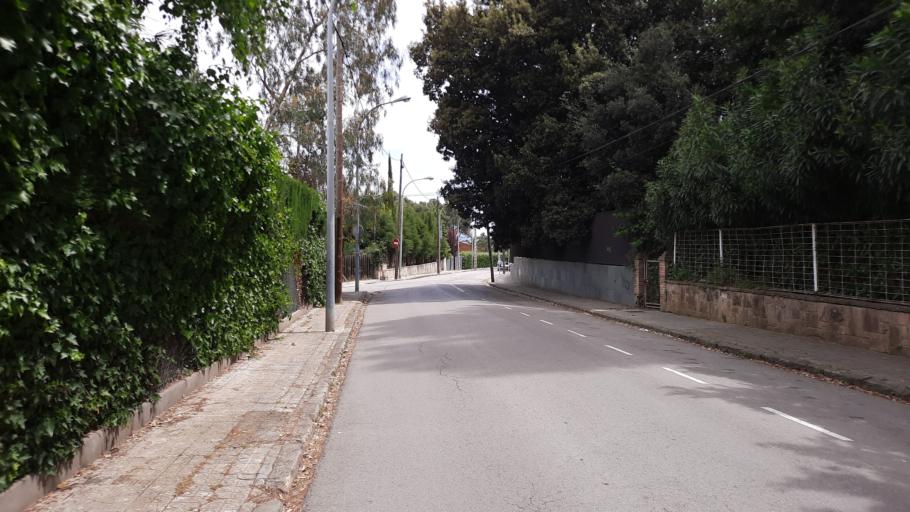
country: ES
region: Catalonia
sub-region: Provincia de Barcelona
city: Sant Quirze del Valles
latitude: 41.5054
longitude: 2.0847
